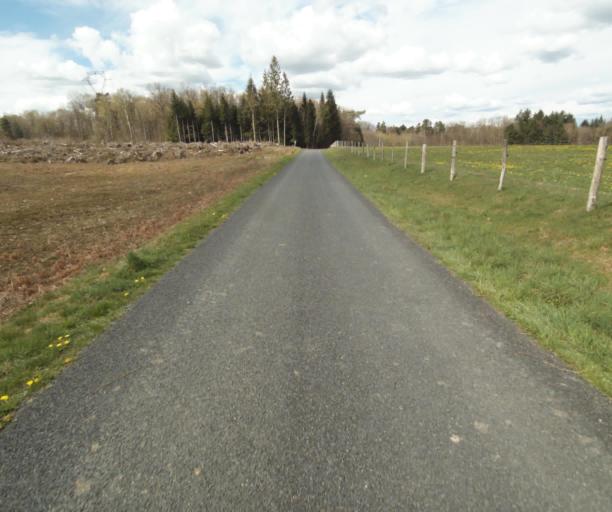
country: FR
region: Limousin
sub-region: Departement de la Correze
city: Argentat
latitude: 45.2048
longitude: 1.9039
